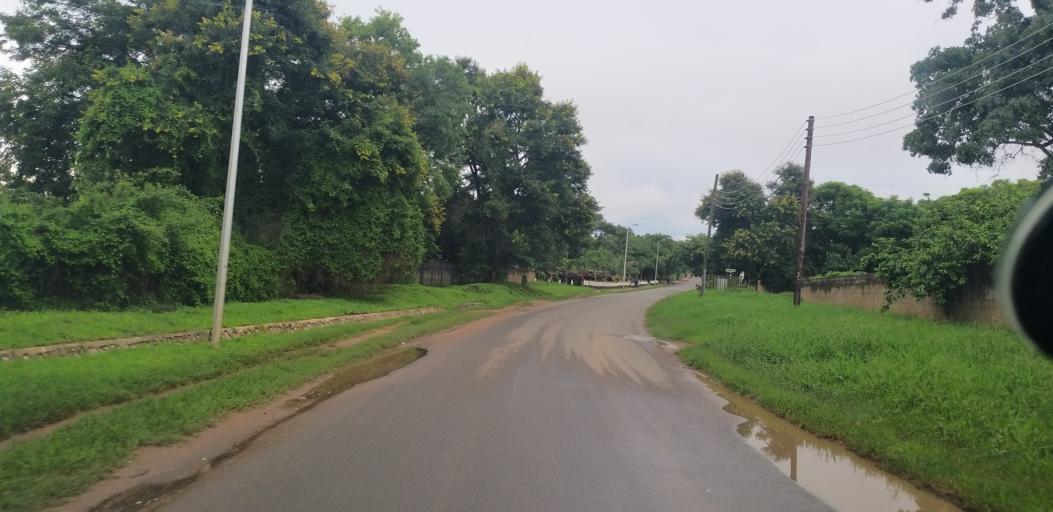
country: ZM
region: Lusaka
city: Lusaka
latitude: -15.4280
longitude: 28.3329
